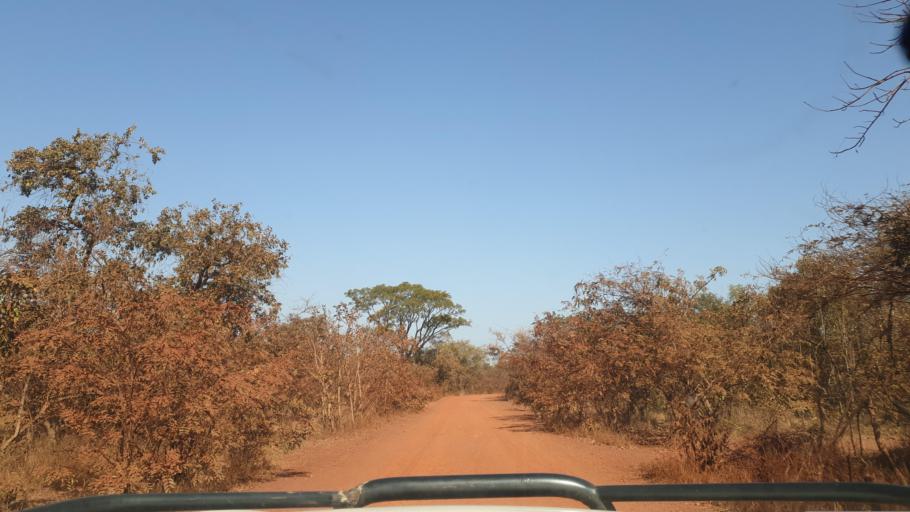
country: ML
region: Koulikoro
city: Dioila
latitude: 11.8482
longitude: -6.9787
